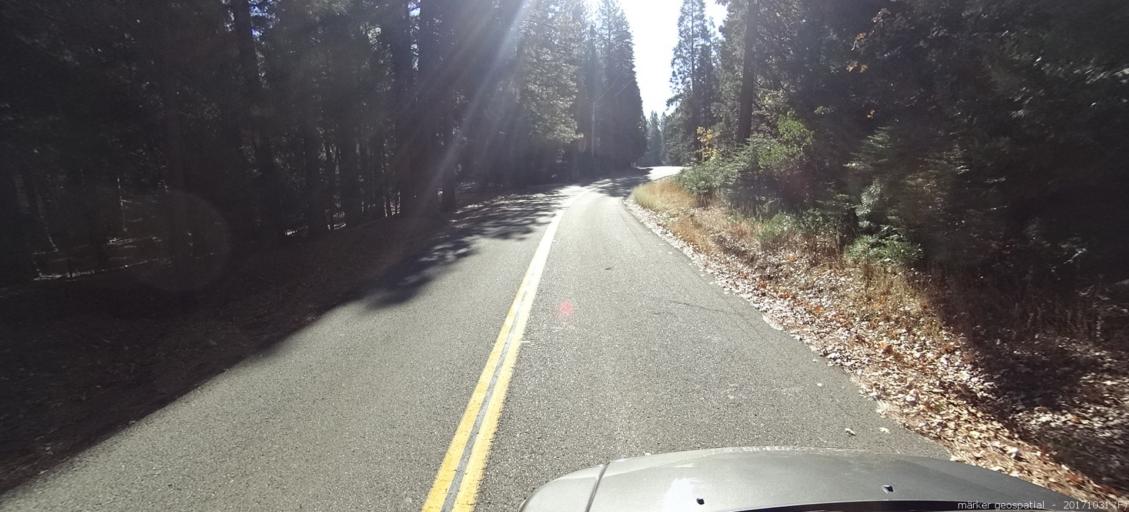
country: US
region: California
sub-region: Shasta County
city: Shingletown
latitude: 40.4896
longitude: -121.8857
